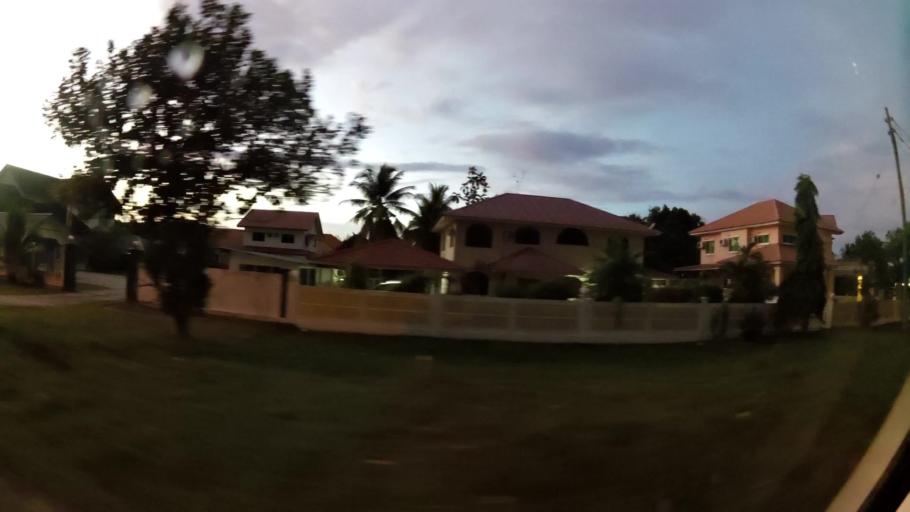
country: BN
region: Belait
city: Seria
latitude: 4.6524
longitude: 114.4259
